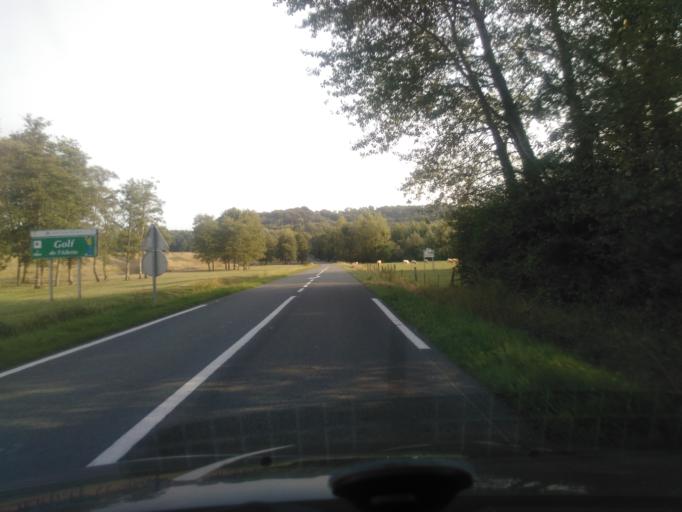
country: FR
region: Picardie
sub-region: Departement de l'Aisne
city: Bruyeres-et-Montberault
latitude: 49.4668
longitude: 3.6652
